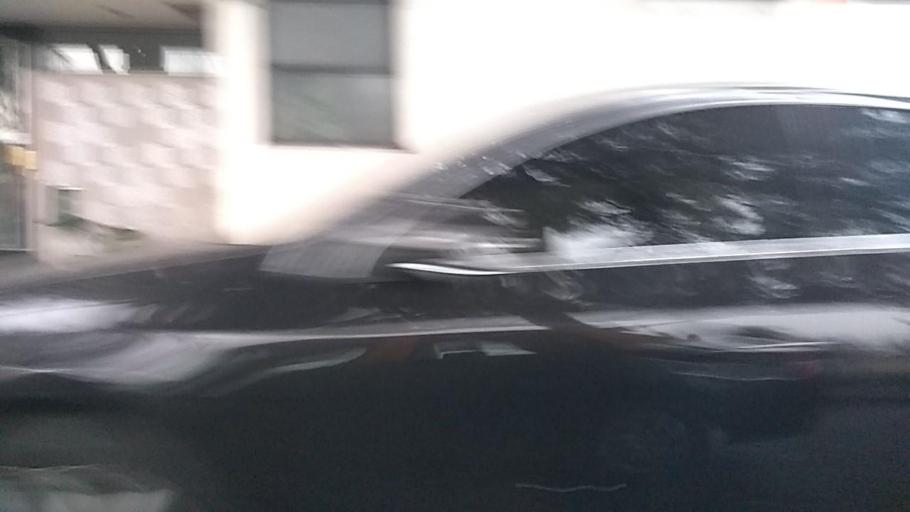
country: AR
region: Buenos Aires F.D.
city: Villa Santa Rita
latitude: -34.6016
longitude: -58.5003
